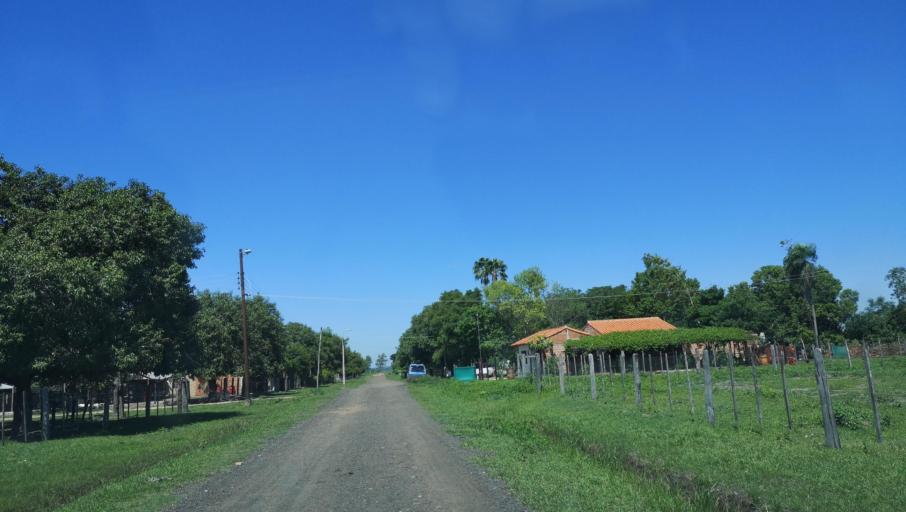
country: PY
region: Caaguazu
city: Carayao
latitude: -25.1924
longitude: -56.4051
